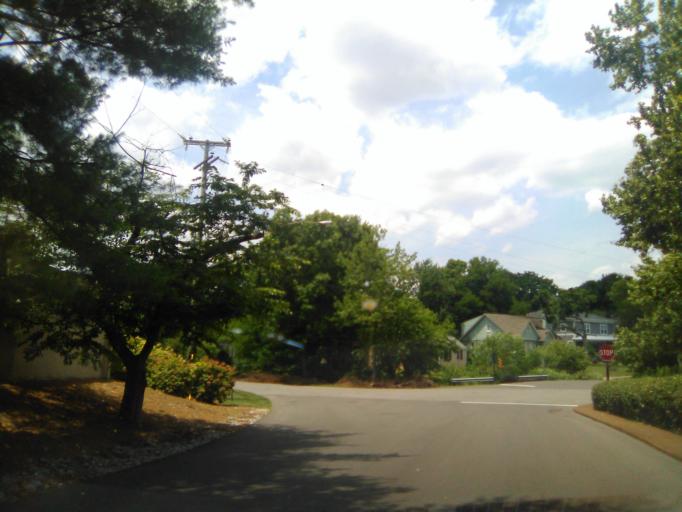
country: US
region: Tennessee
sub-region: Davidson County
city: Belle Meade
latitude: 36.1277
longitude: -86.8290
